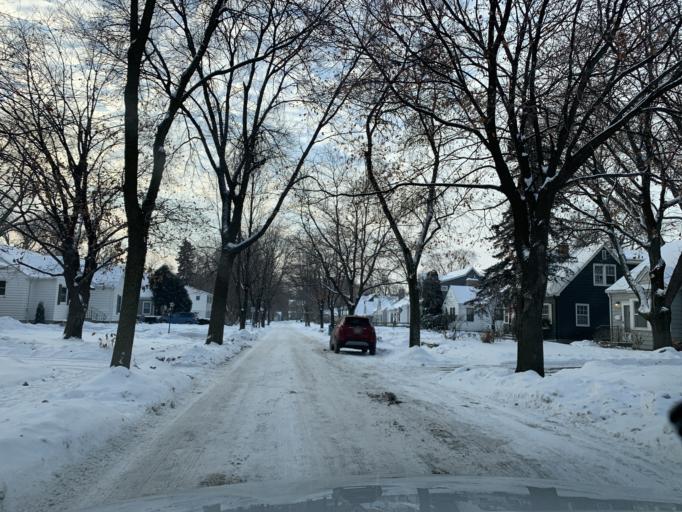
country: US
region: Minnesota
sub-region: Hennepin County
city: Saint Louis Park
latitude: 44.9261
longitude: -93.3520
